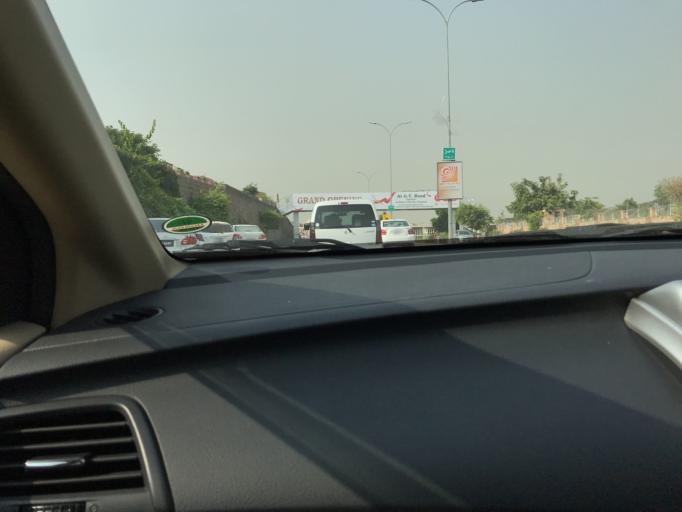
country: PK
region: Punjab
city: Rawalpindi
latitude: 33.5402
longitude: 73.0979
